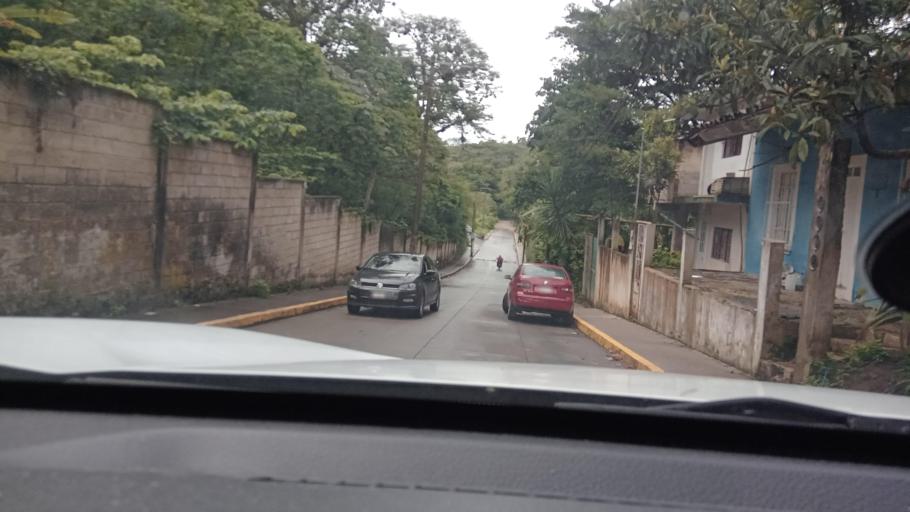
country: MX
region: Veracruz
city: Coatepec
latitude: 19.4448
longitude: -96.9592
